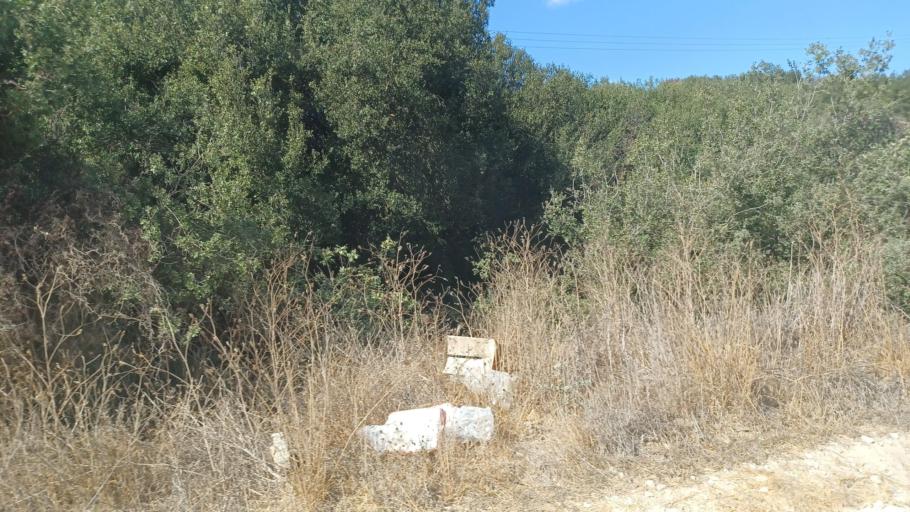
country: CY
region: Pafos
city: Mesogi
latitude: 34.8420
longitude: 32.5484
